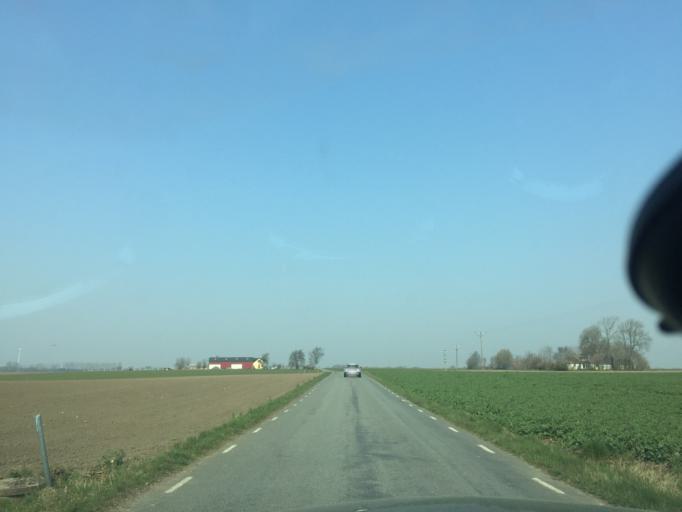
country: SE
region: Skane
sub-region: Simrishamns Kommun
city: Simrishamn
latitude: 55.4548
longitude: 14.2144
